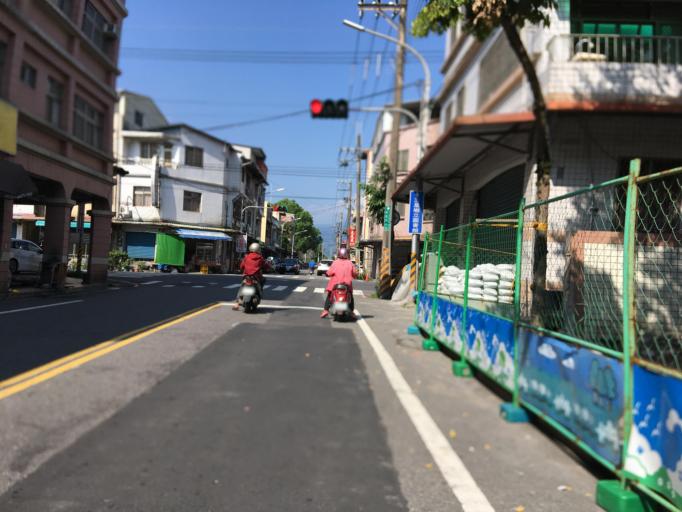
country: TW
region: Taiwan
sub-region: Yilan
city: Yilan
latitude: 24.6675
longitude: 121.6528
